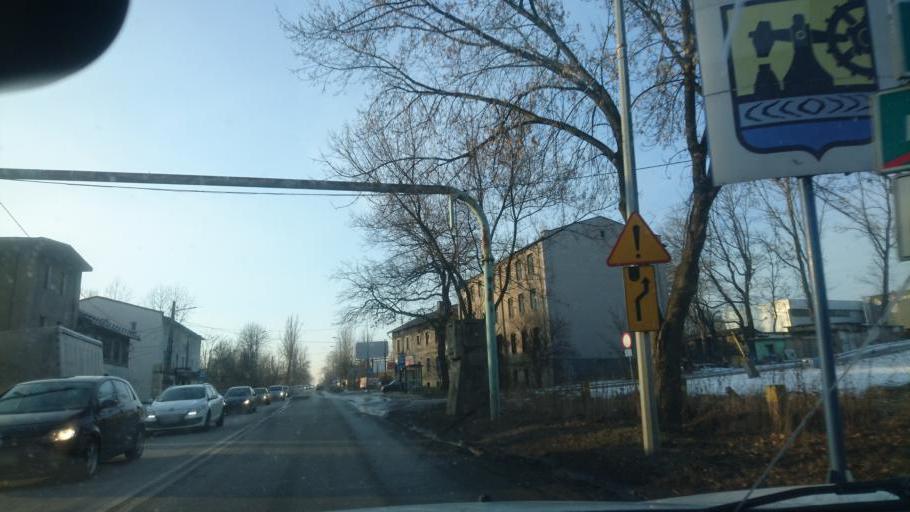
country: PL
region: Silesian Voivodeship
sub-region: Sosnowiec
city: Sosnowiec
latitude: 50.2506
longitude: 19.1109
